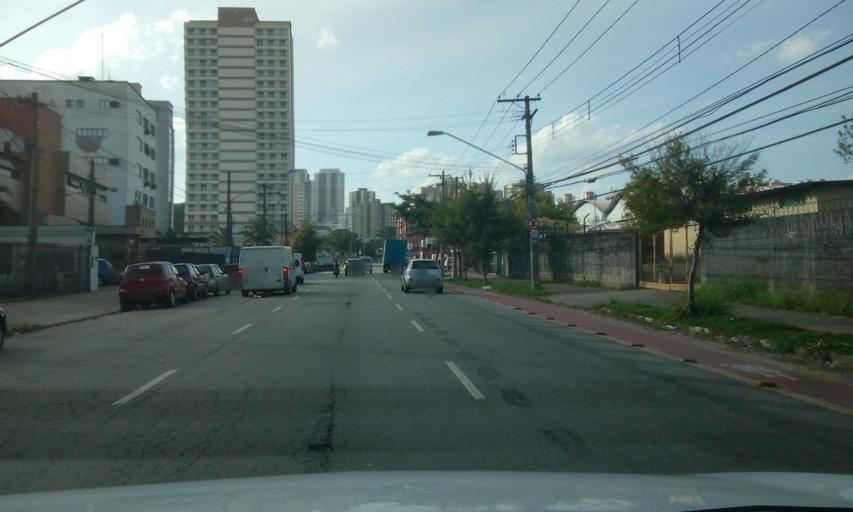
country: BR
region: Sao Paulo
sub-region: Sao Paulo
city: Sao Paulo
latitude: -23.5064
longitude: -46.6801
